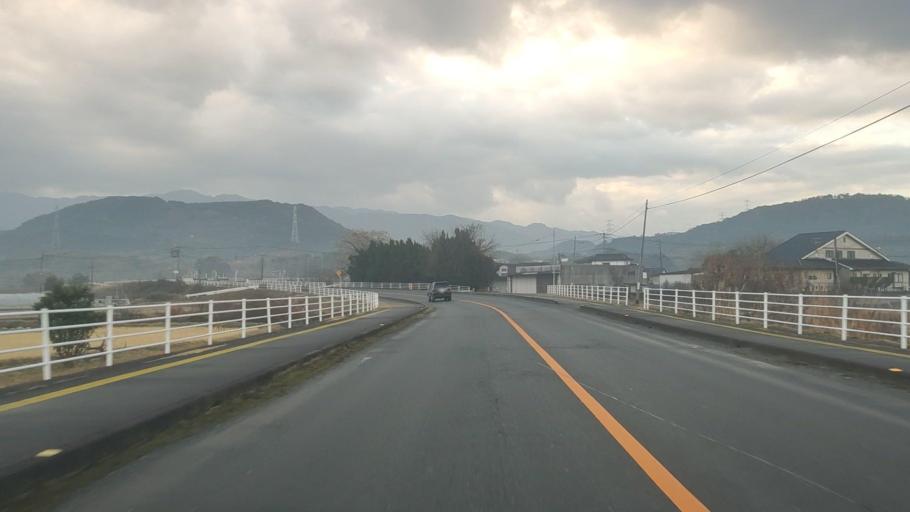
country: JP
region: Kumamoto
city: Matsubase
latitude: 32.6457
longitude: 130.8117
